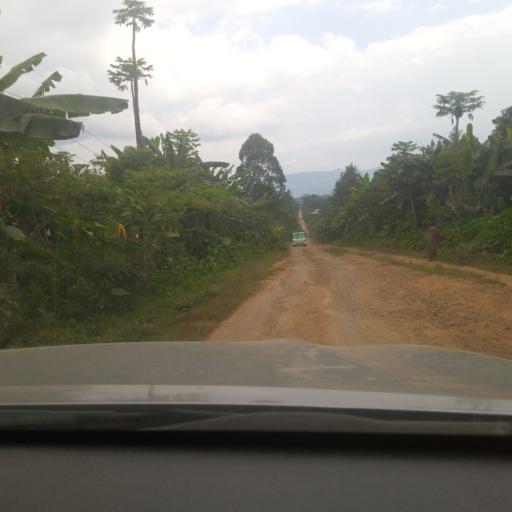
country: ET
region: Southern Nations, Nationalities, and People's Region
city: Tippi
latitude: 7.1403
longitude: 35.4197
